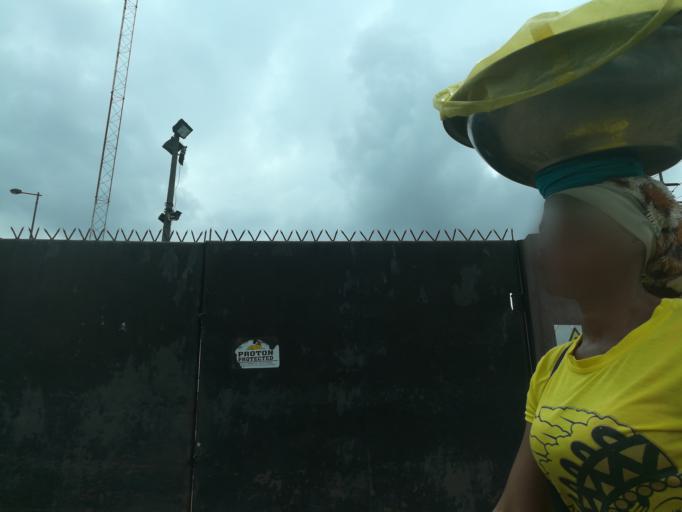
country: NG
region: Lagos
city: Ojota
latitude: 6.6049
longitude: 3.4004
